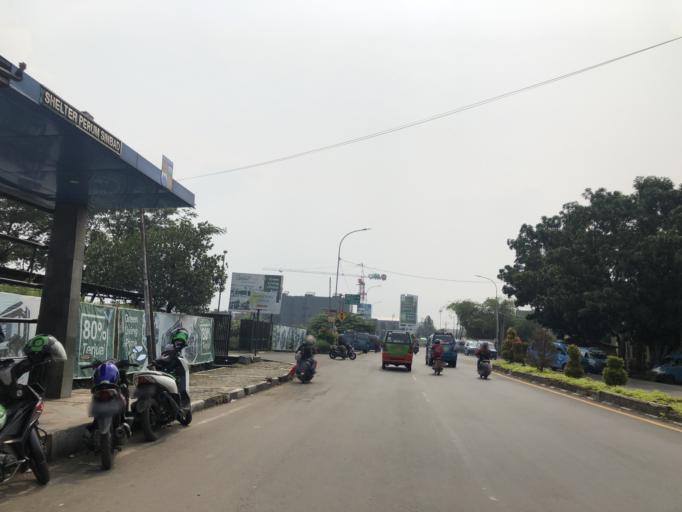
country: ID
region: West Java
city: Bogor
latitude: -6.5726
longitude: 106.7530
